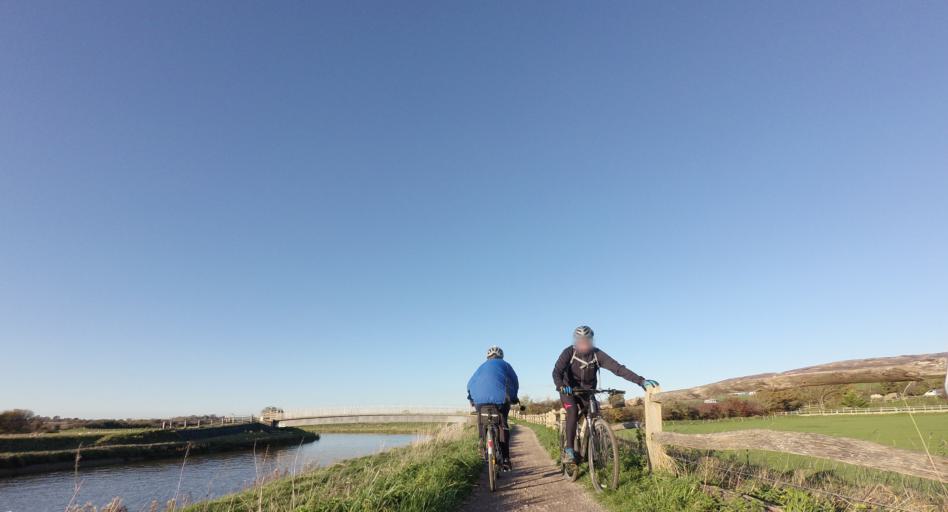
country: GB
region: England
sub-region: West Sussex
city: Steyning
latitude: 50.8700
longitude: -0.3009
